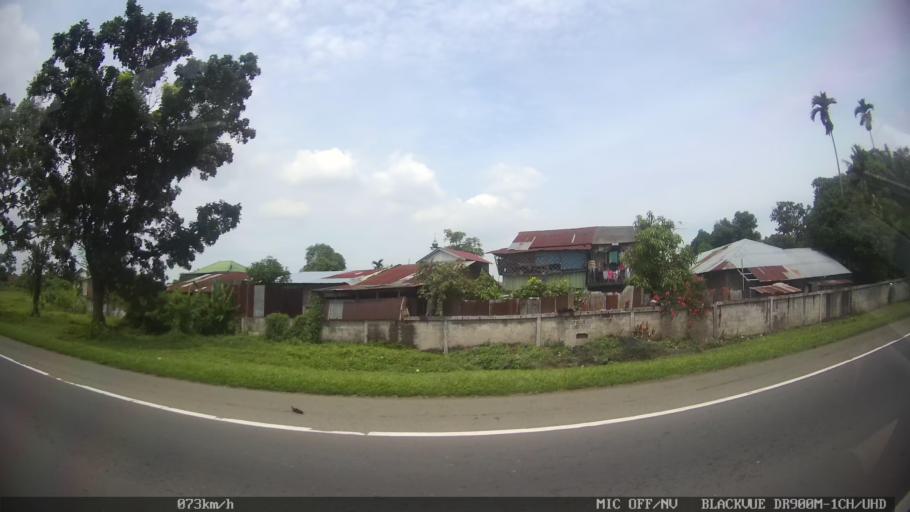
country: ID
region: North Sumatra
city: Labuhan Deli
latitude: 3.6944
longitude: 98.6818
